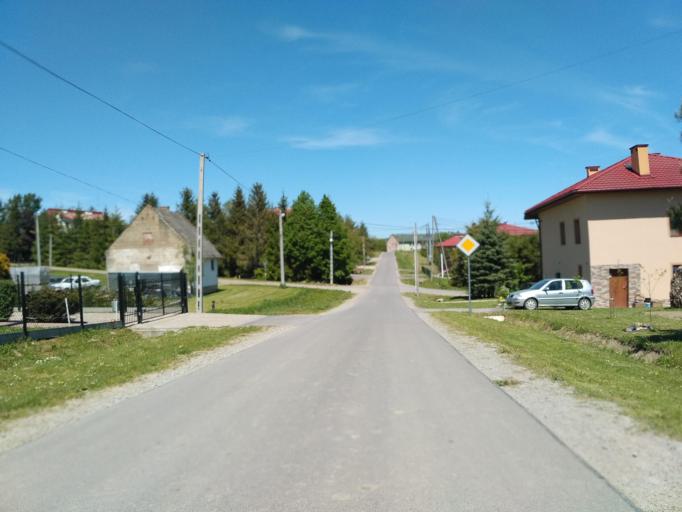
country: PL
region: Subcarpathian Voivodeship
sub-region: Powiat sanocki
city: Bukowsko
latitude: 49.5059
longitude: 22.0304
